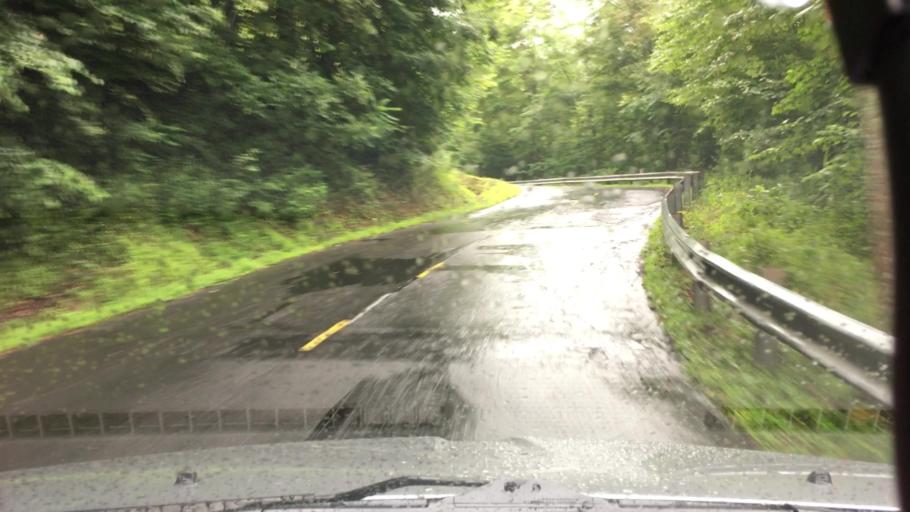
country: US
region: North Carolina
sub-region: Madison County
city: Mars Hill
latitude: 35.9452
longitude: -82.5249
